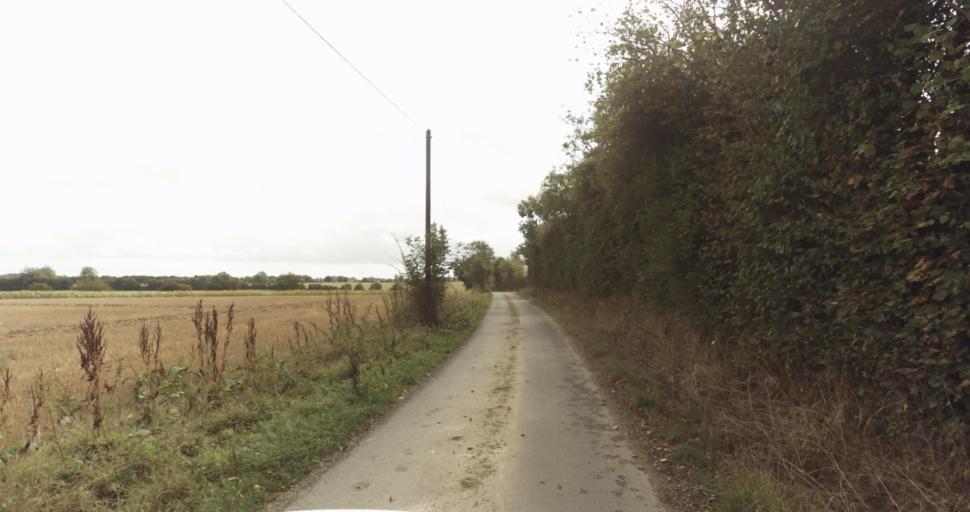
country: FR
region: Lower Normandy
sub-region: Departement de l'Orne
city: Gace
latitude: 48.8068
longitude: 0.3590
